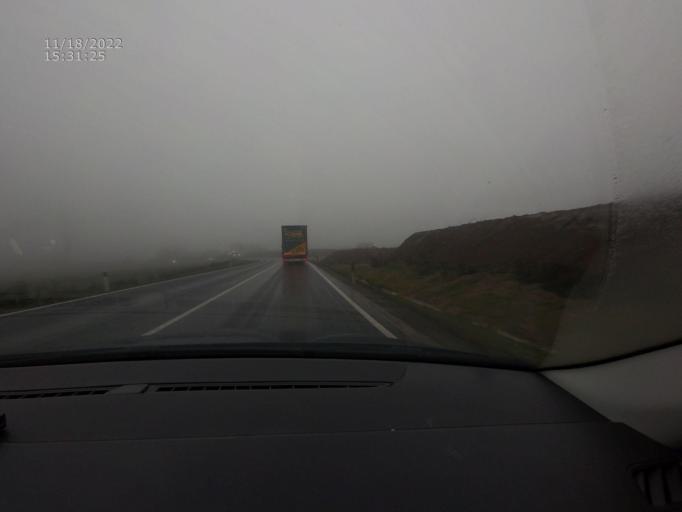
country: CZ
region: Central Bohemia
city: Milin
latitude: 49.6541
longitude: 14.0554
